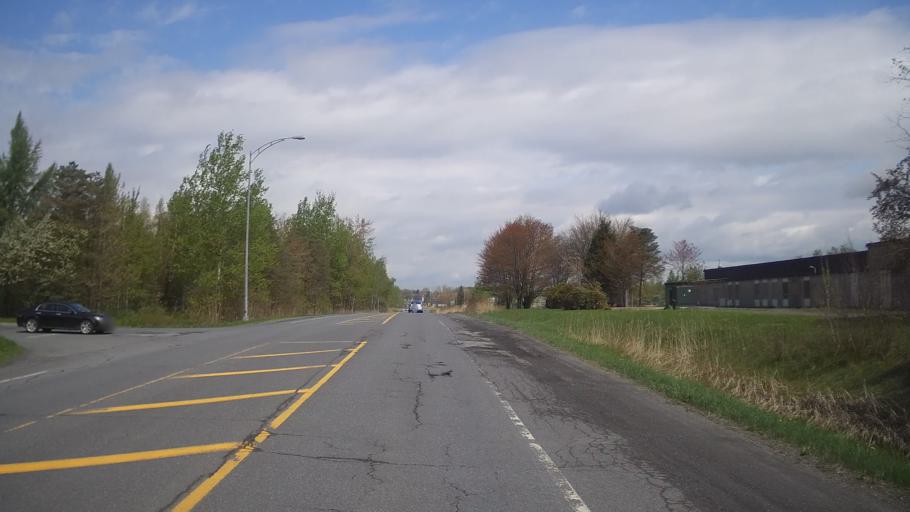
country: CA
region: Quebec
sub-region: Monteregie
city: Cowansville
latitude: 45.1994
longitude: -72.7638
